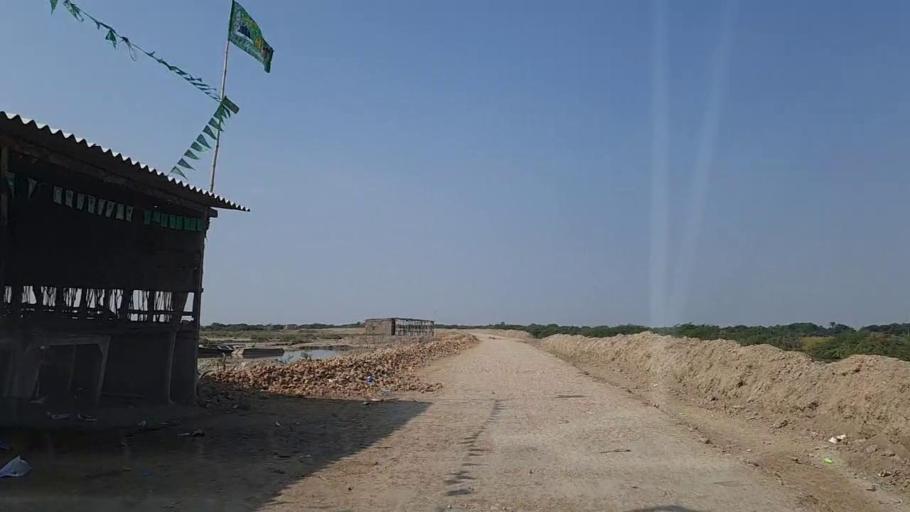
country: PK
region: Sindh
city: Chuhar Jamali
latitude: 24.1964
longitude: 67.8373
